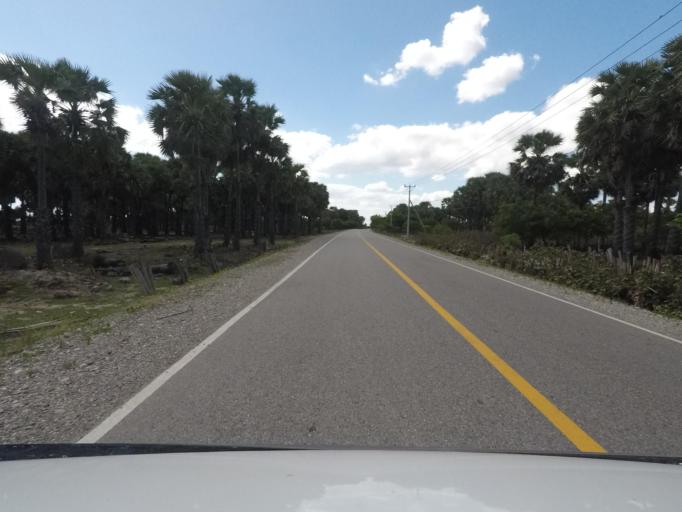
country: TL
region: Baucau
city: Baucau
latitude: -8.4327
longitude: 126.6756
